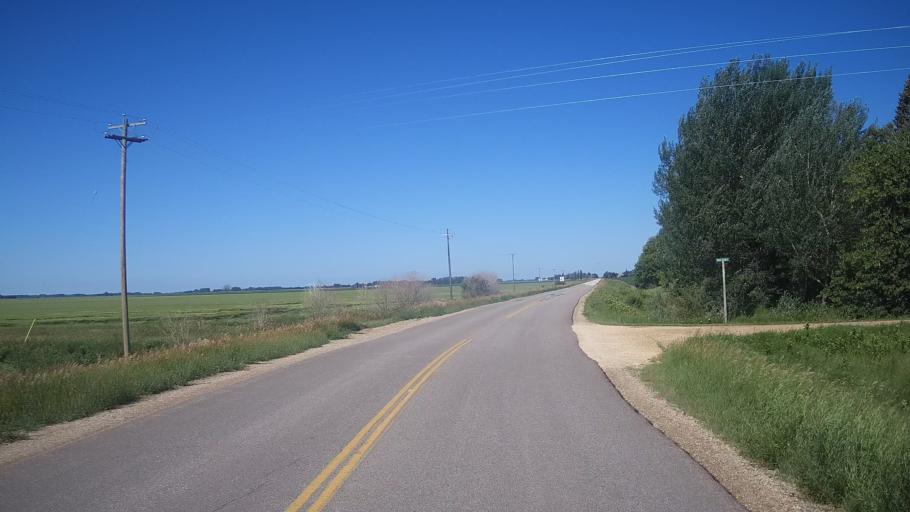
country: CA
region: Manitoba
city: Portage la Prairie
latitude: 50.0438
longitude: -98.0329
